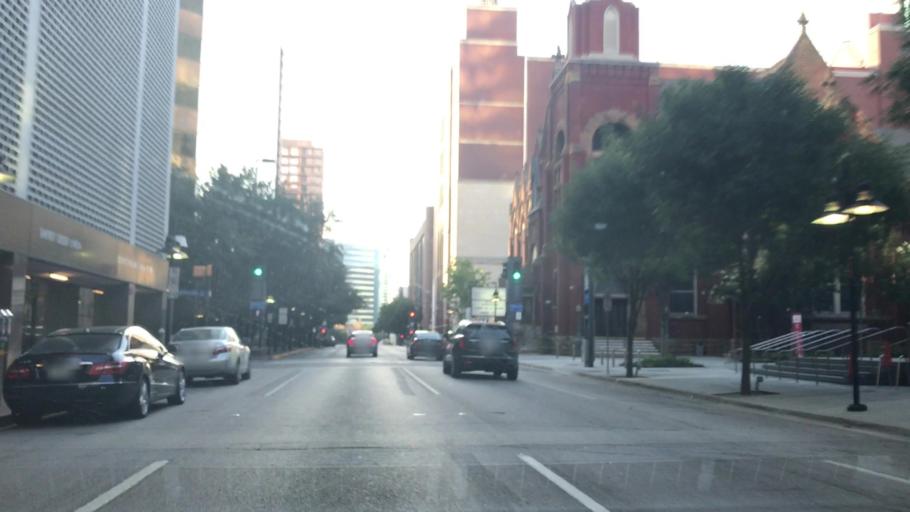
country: US
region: Texas
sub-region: Dallas County
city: Dallas
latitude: 32.7841
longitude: -96.7993
